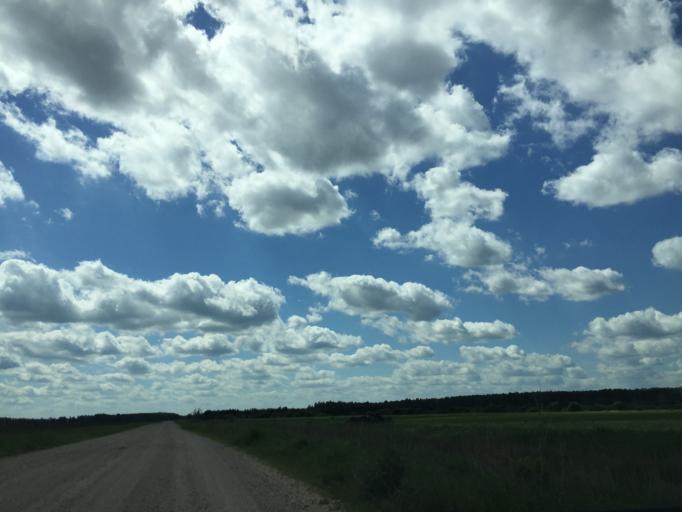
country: LV
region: Olaine
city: Olaine
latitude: 56.8665
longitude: 23.9551
